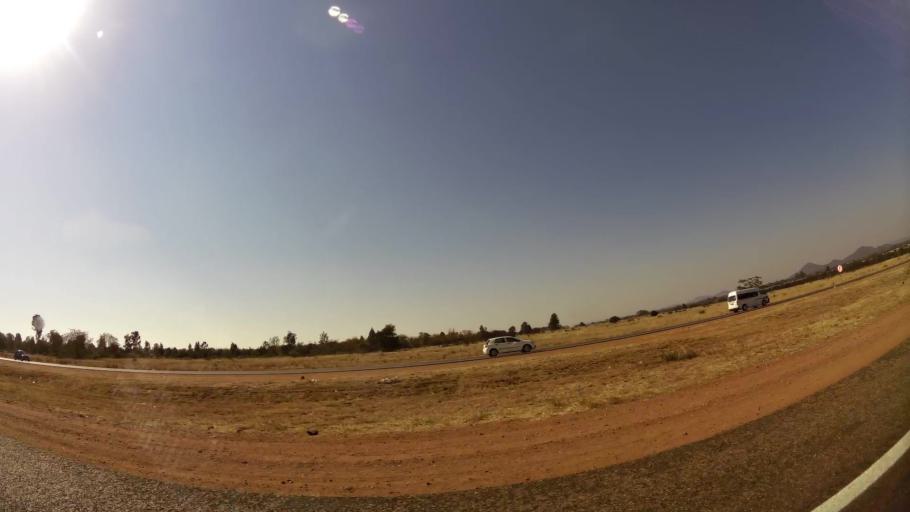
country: ZA
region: Gauteng
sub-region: City of Tshwane Metropolitan Municipality
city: Mabopane
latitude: -25.5872
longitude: 28.1114
